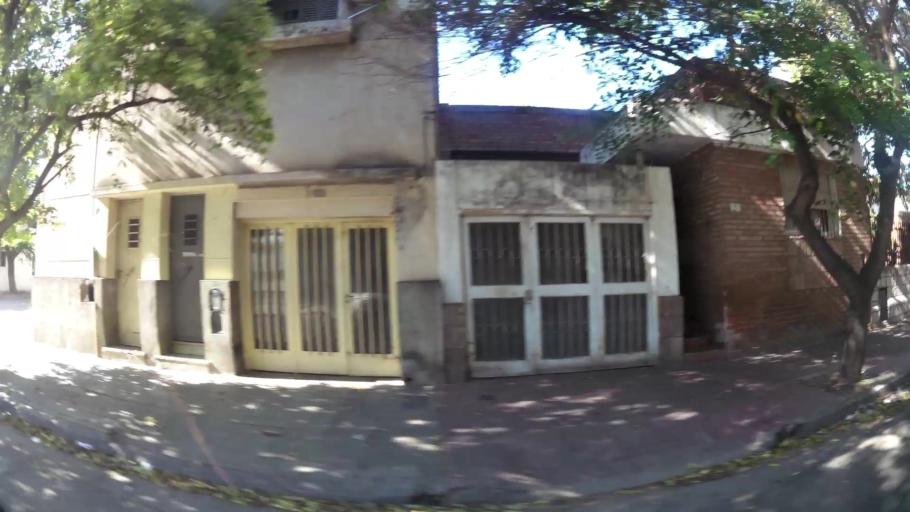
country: AR
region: Cordoba
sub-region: Departamento de Capital
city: Cordoba
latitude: -31.4258
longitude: -64.1461
